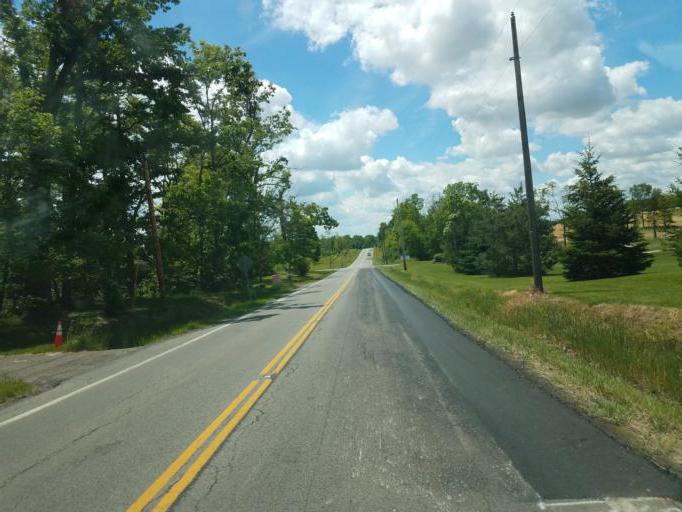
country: US
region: Ohio
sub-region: Richland County
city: Lexington
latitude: 40.6457
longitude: -82.5917
